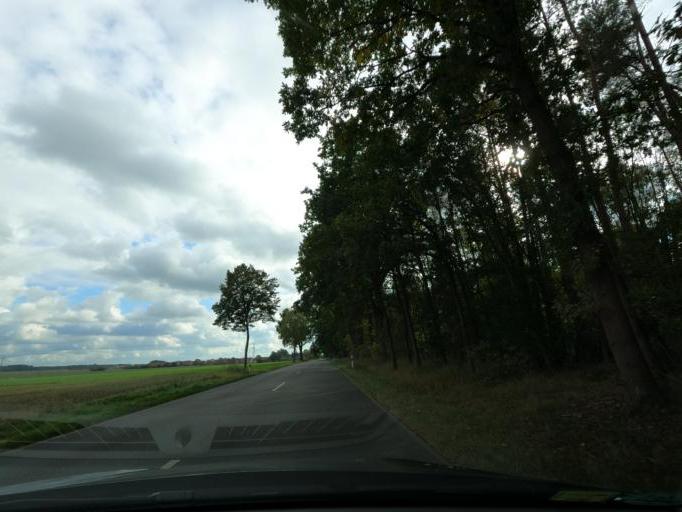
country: DE
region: Lower Saxony
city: Klein Schwulper
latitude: 52.3645
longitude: 10.4274
